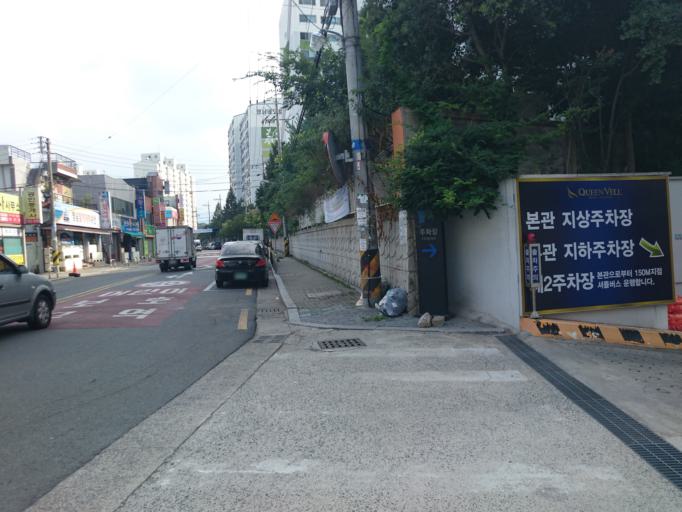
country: KR
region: Daegu
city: Daegu
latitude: 35.8818
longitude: 128.6622
